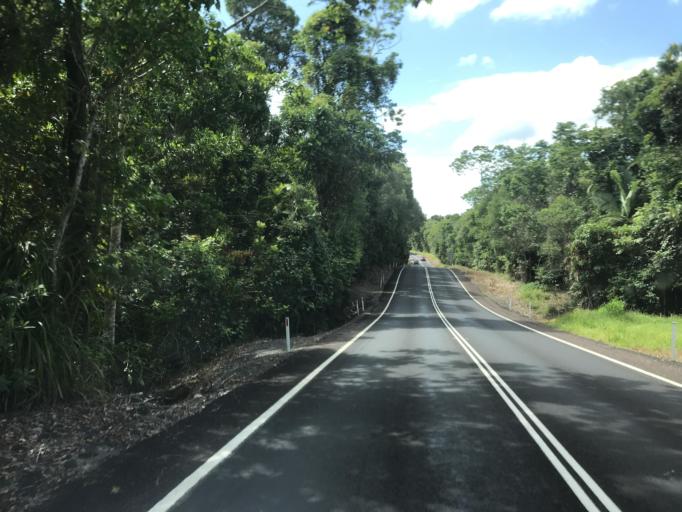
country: AU
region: Queensland
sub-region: Cassowary Coast
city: Innisfail
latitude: -17.8632
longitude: 146.0657
